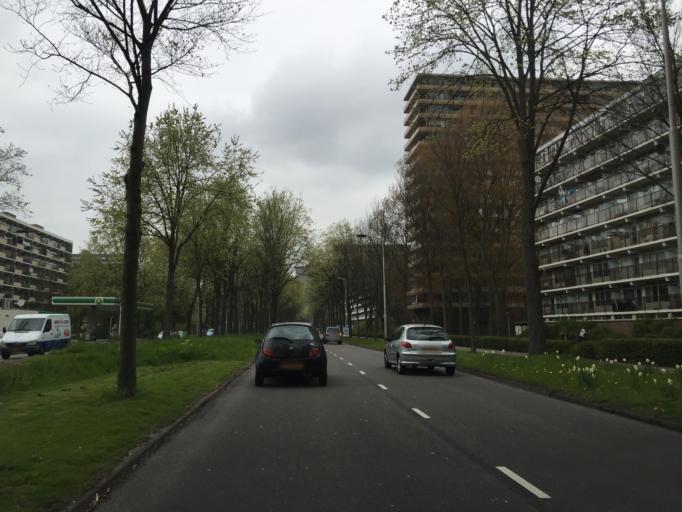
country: NL
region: South Holland
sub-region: Gemeente Delft
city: Delft
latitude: 51.9911
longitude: 4.3577
